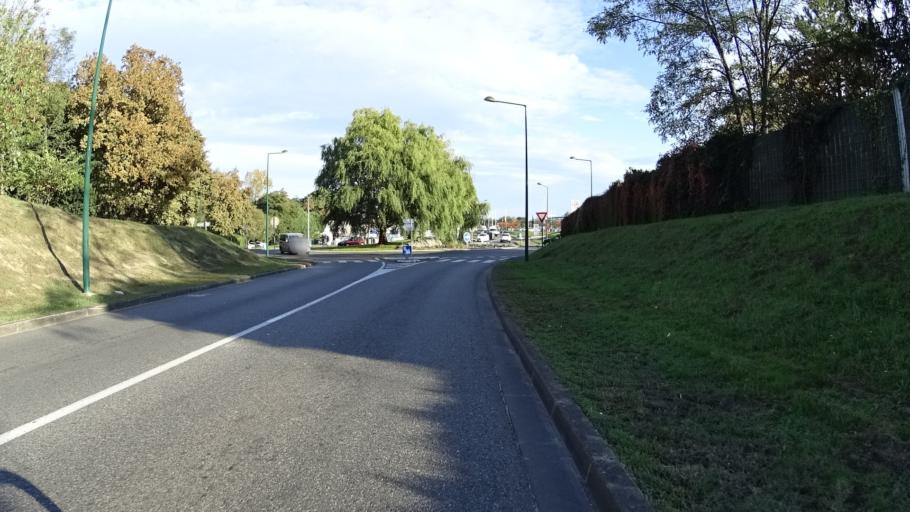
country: FR
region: Aquitaine
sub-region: Departement des Landes
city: Saint-Paul-les-Dax
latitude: 43.7331
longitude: -1.0453
